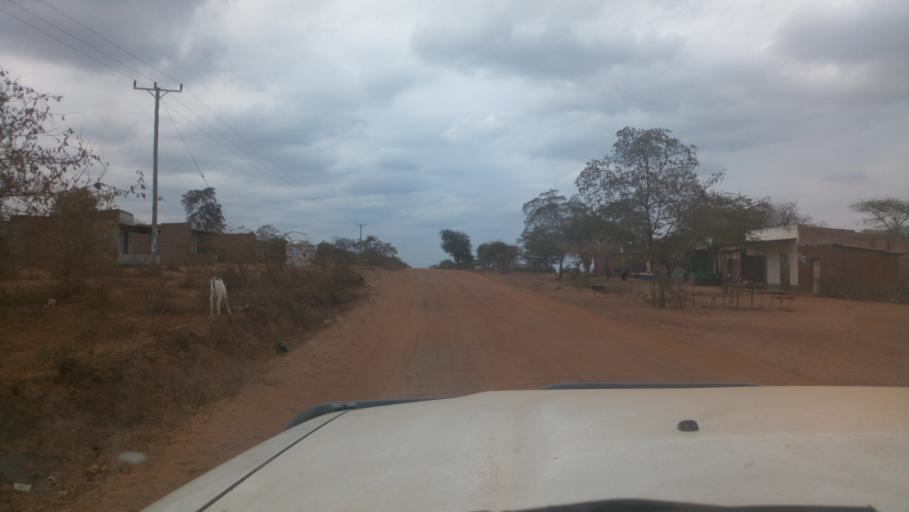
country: KE
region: Kitui
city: Kitui
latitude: -1.5739
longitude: 37.9169
